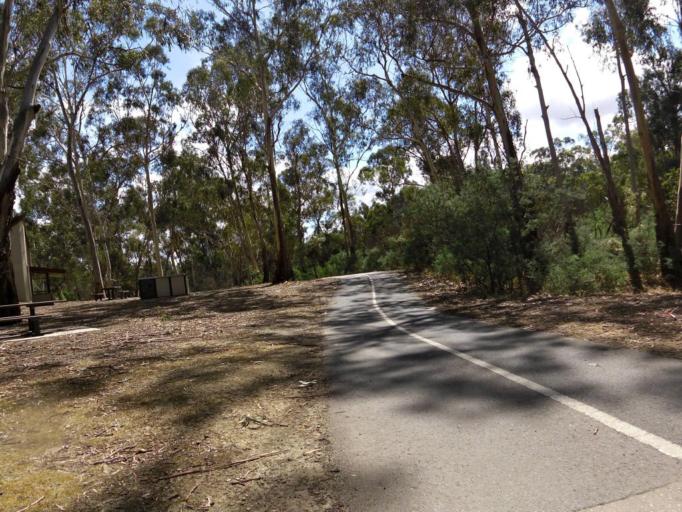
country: AU
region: Victoria
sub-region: Nillumbik
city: Eltham North
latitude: -37.6961
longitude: 145.1506
